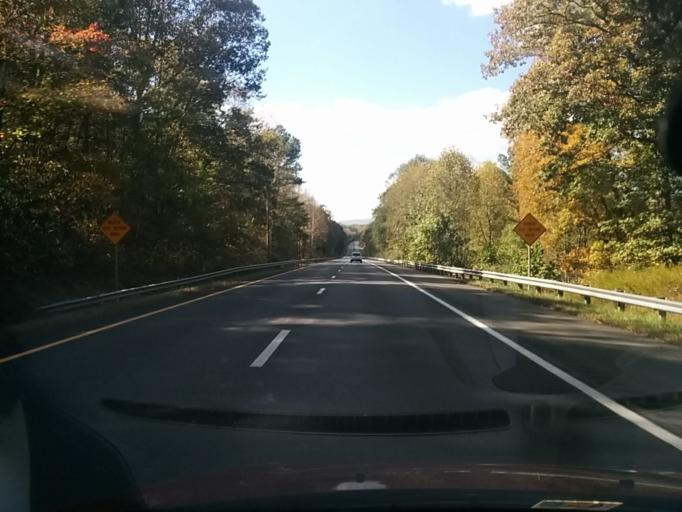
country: US
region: Virginia
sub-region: Albemarle County
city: Crozet
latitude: 38.0311
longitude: -78.6674
